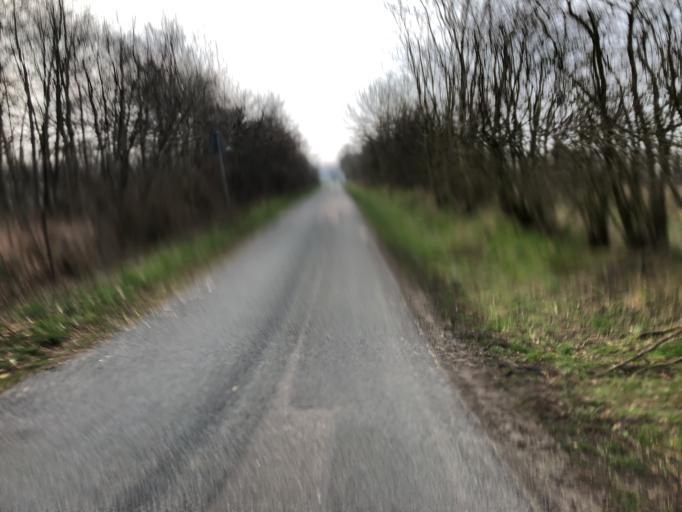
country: DE
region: Schleswig-Holstein
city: Wanderup
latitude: 54.7011
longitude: 9.3481
